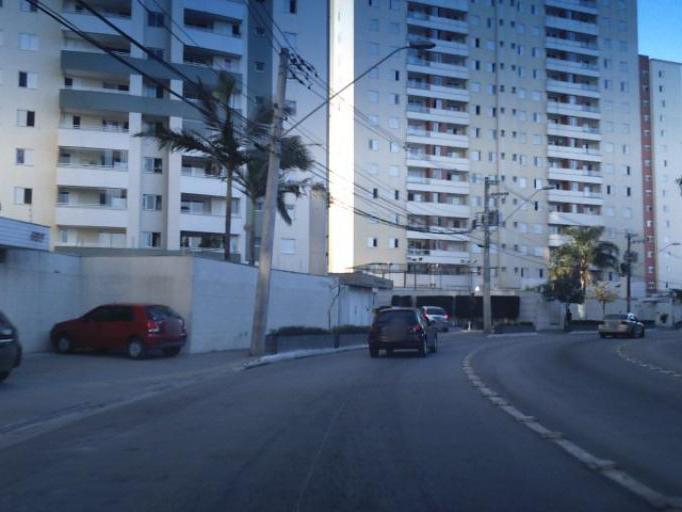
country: BR
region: Sao Paulo
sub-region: Sao Jose Dos Campos
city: Sao Jose dos Campos
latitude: -23.1657
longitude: -45.8928
